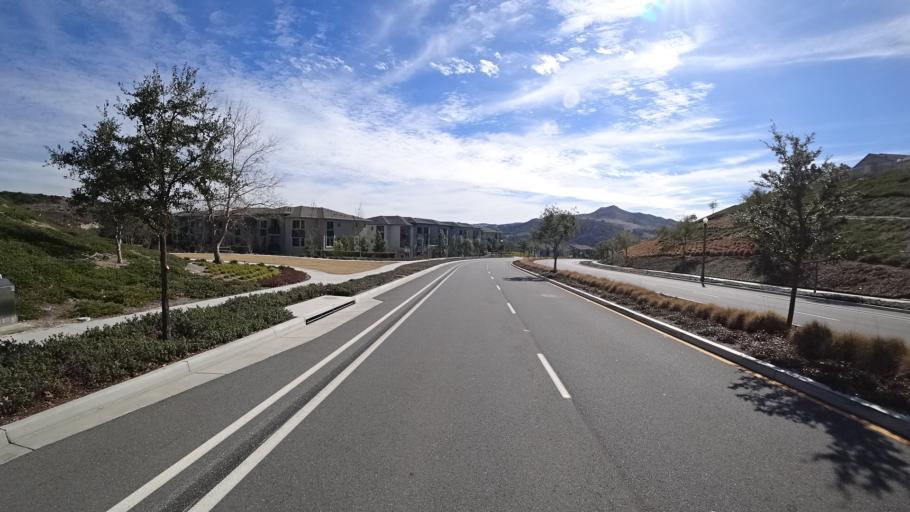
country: US
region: California
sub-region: Orange County
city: Ladera Ranch
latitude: 33.5325
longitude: -117.6003
